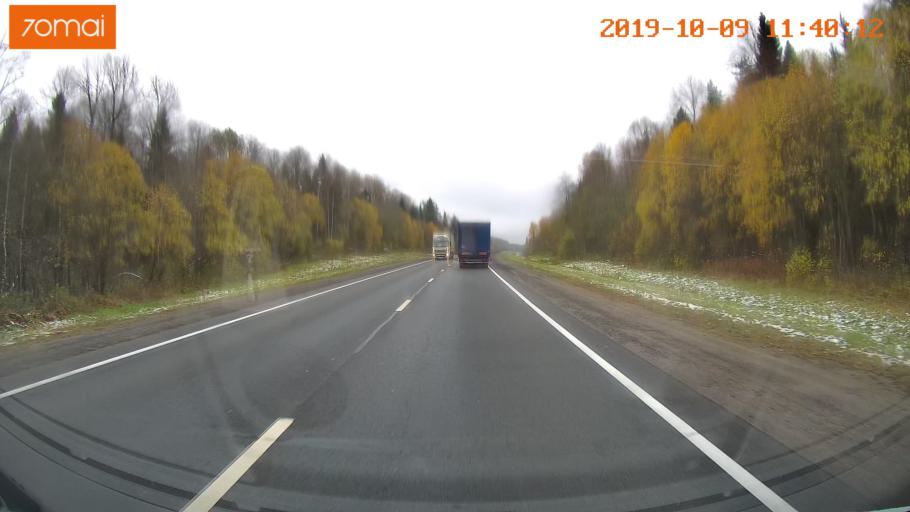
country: RU
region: Vologda
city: Gryazovets
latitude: 58.9458
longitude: 40.1731
